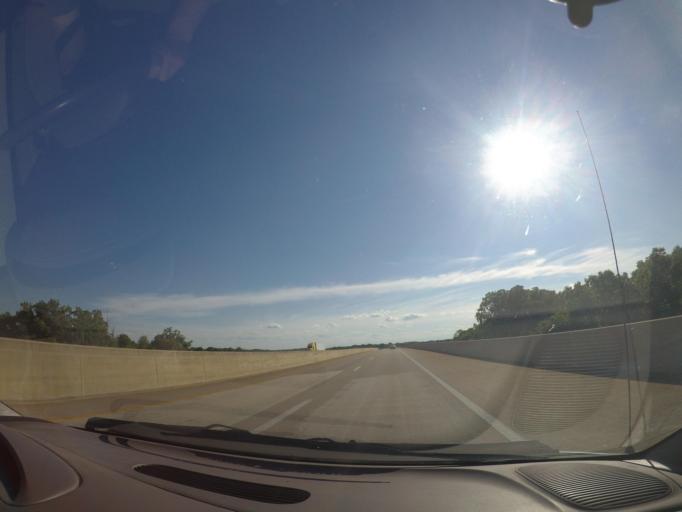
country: US
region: Ohio
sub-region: Henry County
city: Liberty Center
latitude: 41.4199
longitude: -84.0319
